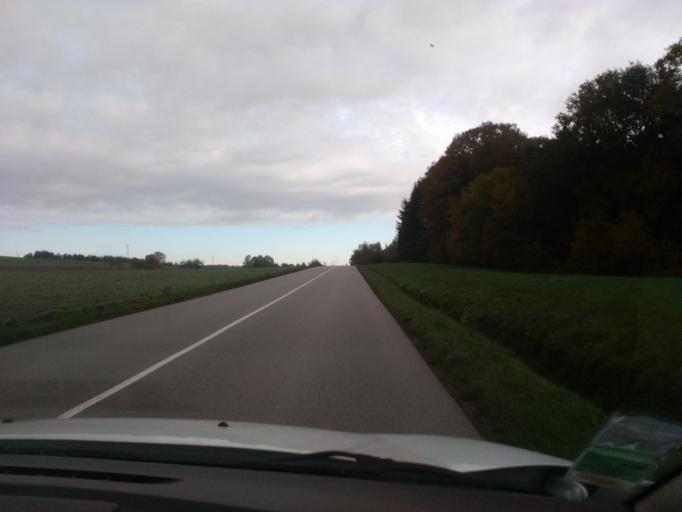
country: FR
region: Lorraine
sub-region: Departement des Vosges
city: Jeanmenil
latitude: 48.3535
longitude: 6.7190
